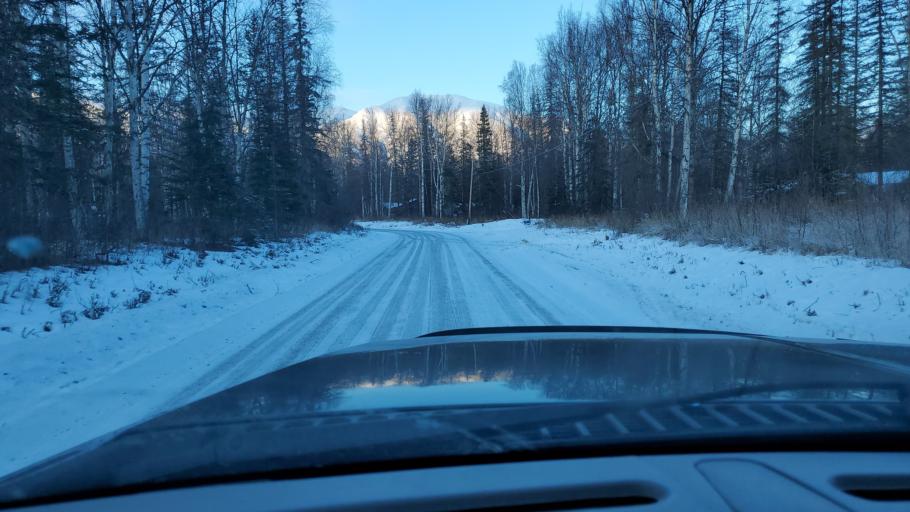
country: US
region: Alaska
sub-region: Matanuska-Susitna Borough
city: Lakes
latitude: 61.6667
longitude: -149.2939
